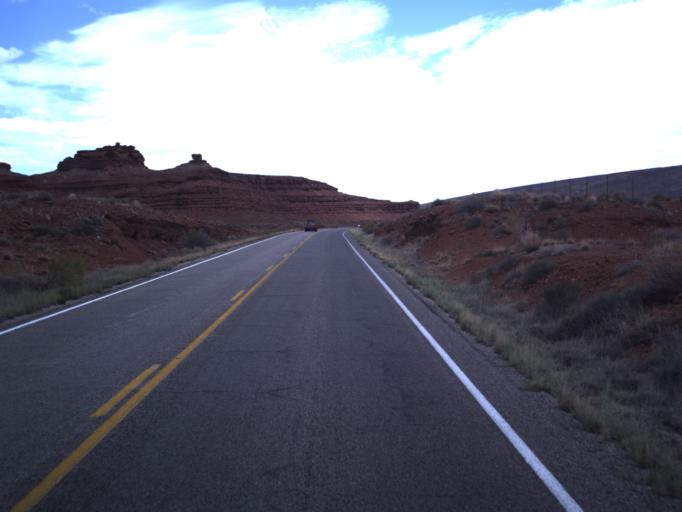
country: US
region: Utah
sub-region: San Juan County
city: Blanding
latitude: 37.2159
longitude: -109.8375
